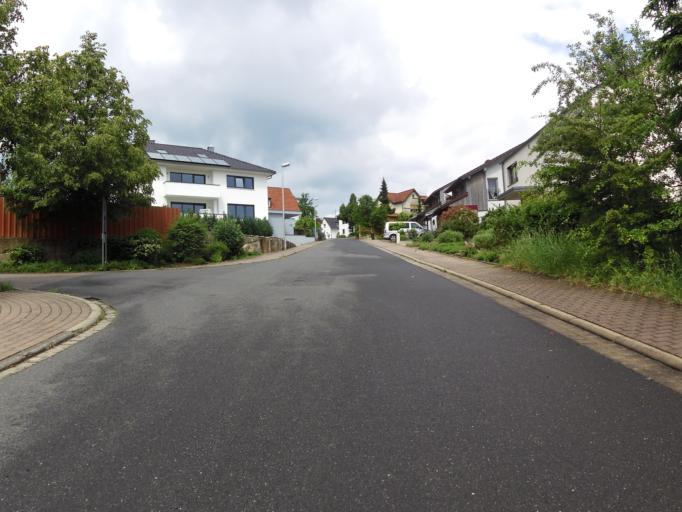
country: DE
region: Bavaria
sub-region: Regierungsbezirk Unterfranken
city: Waldbuttelbrunn
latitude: 49.7842
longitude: 9.8392
